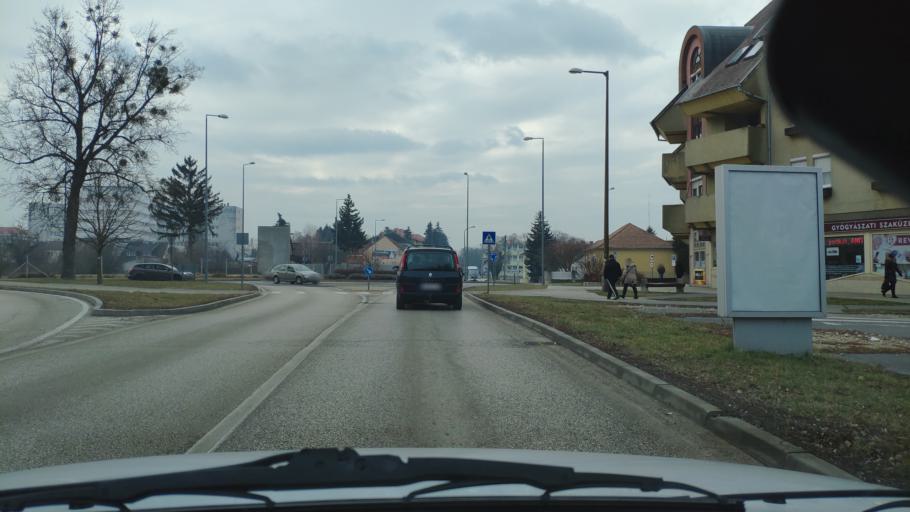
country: HU
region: Zala
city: Nagykanizsa
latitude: 46.4548
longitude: 16.9982
